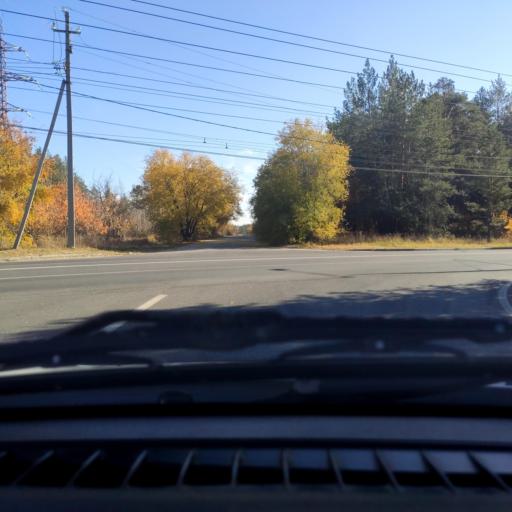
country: RU
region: Samara
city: Zhigulevsk
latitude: 53.5045
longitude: 49.4633
